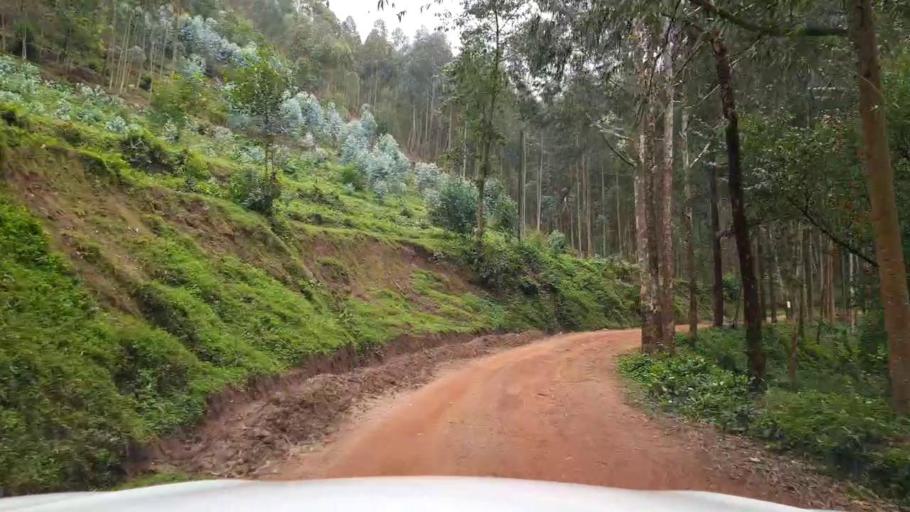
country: UG
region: Western Region
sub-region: Kabale District
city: Kabale
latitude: -1.4238
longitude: 29.8683
